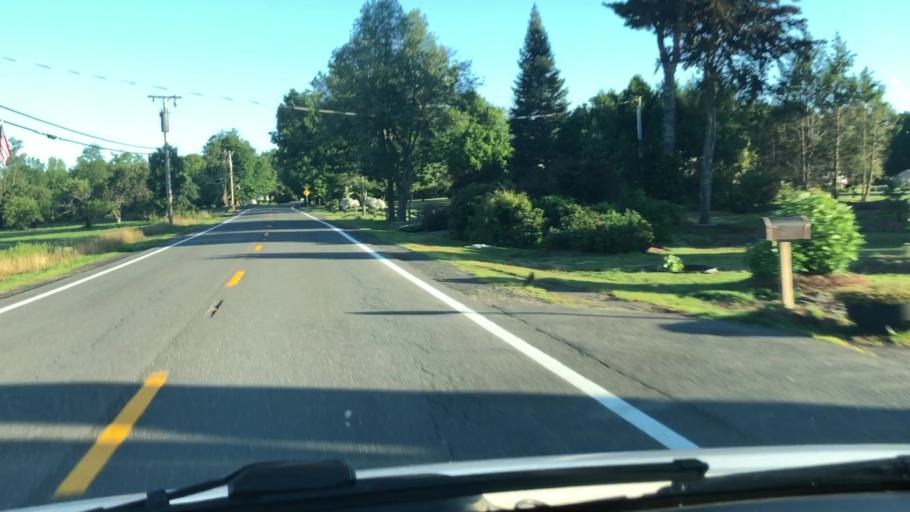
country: US
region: Massachusetts
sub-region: Hampshire County
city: Chesterfield
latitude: 42.3817
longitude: -72.9260
